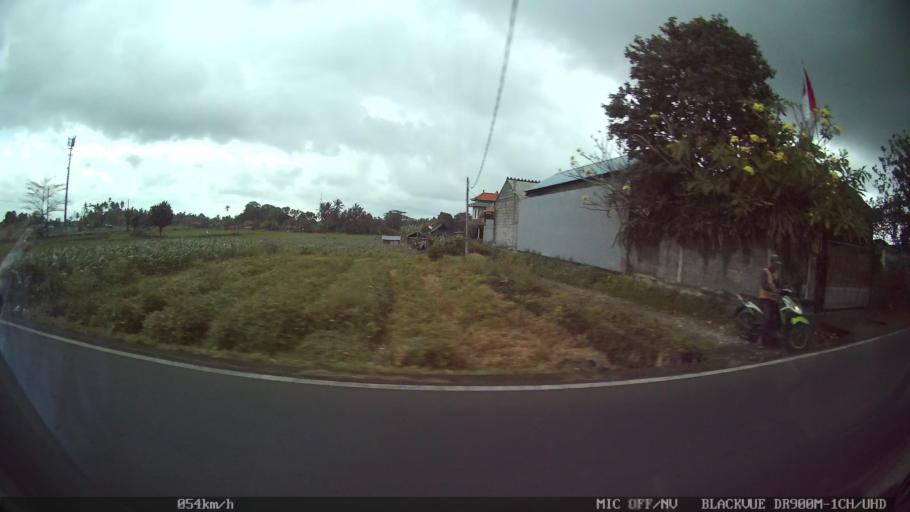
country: ID
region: Bali
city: Banjar Keraman
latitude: -8.5353
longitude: 115.2249
